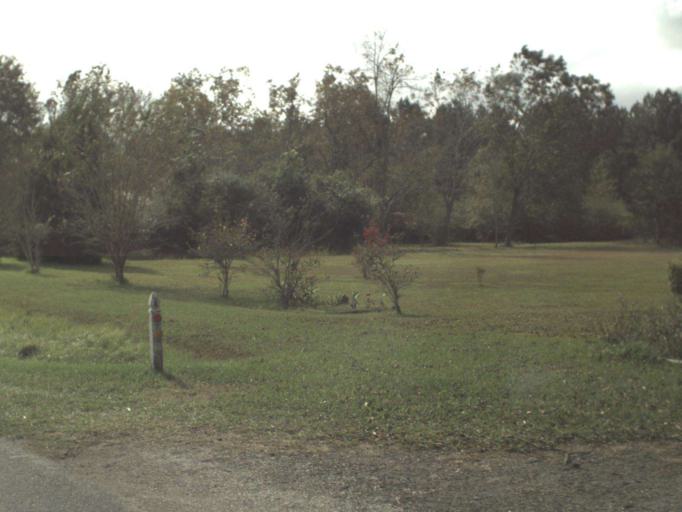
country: US
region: Alabama
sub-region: Escambia County
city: East Brewton
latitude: 30.9969
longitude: -87.0367
